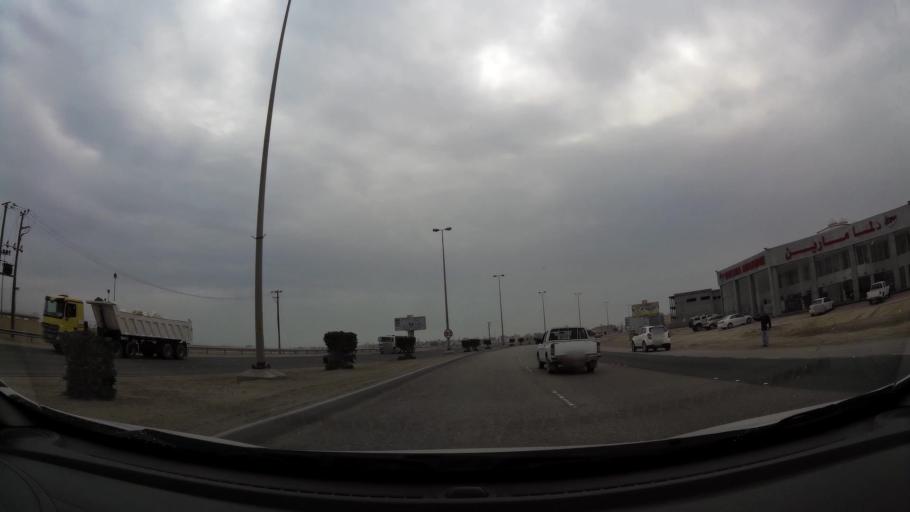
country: BH
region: Northern
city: Sitrah
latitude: 26.1440
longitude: 50.6187
